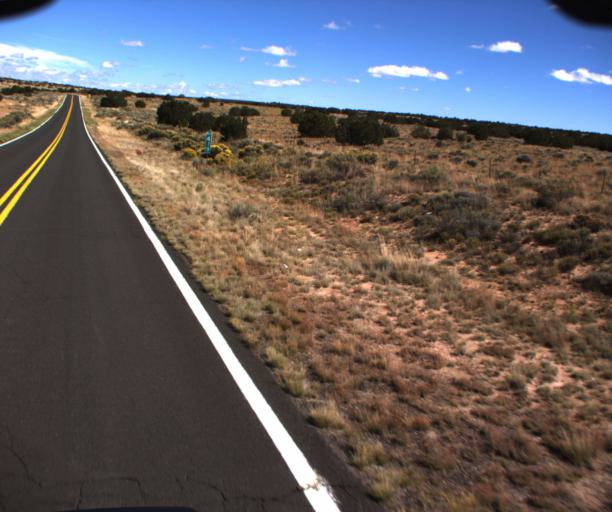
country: US
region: Arizona
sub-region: Apache County
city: Houck
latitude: 34.9244
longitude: -109.2037
